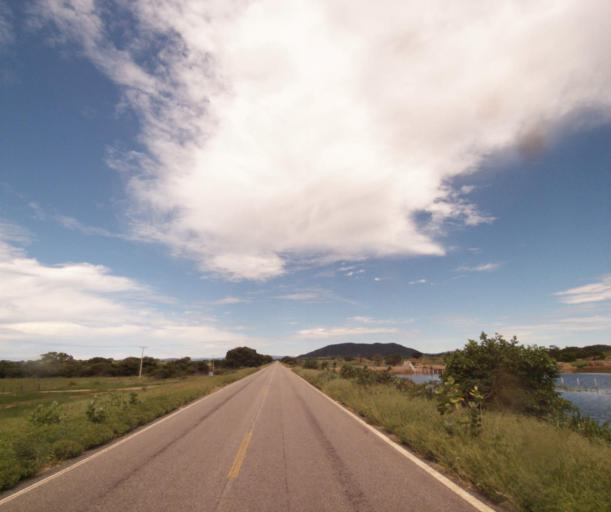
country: BR
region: Bahia
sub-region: Guanambi
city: Guanambi
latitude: -14.2286
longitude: -42.9194
